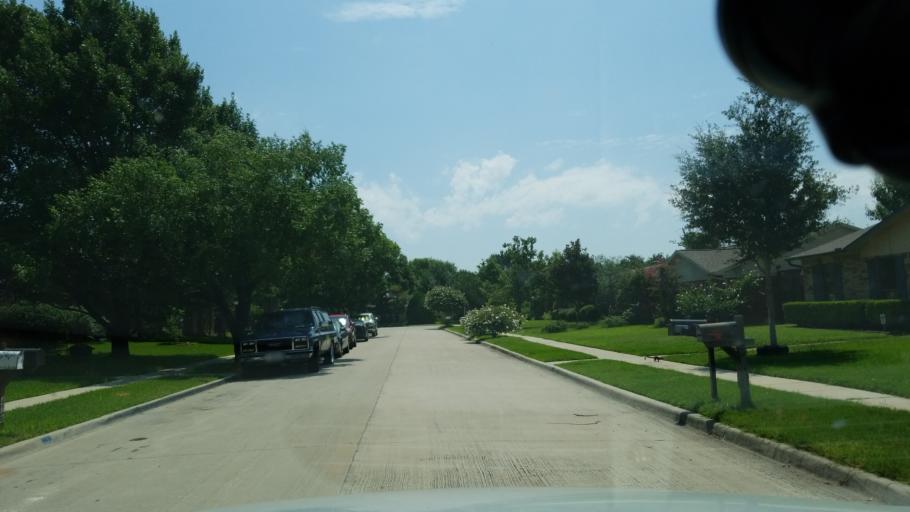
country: US
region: Texas
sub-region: Dallas County
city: Coppell
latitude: 32.9669
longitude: -96.9827
